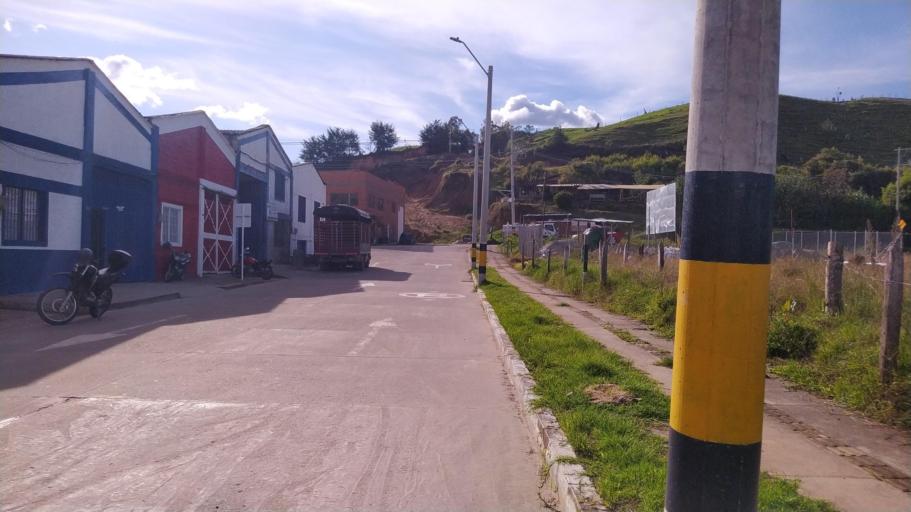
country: CO
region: Antioquia
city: Entrerrios
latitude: 6.5692
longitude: -75.5178
